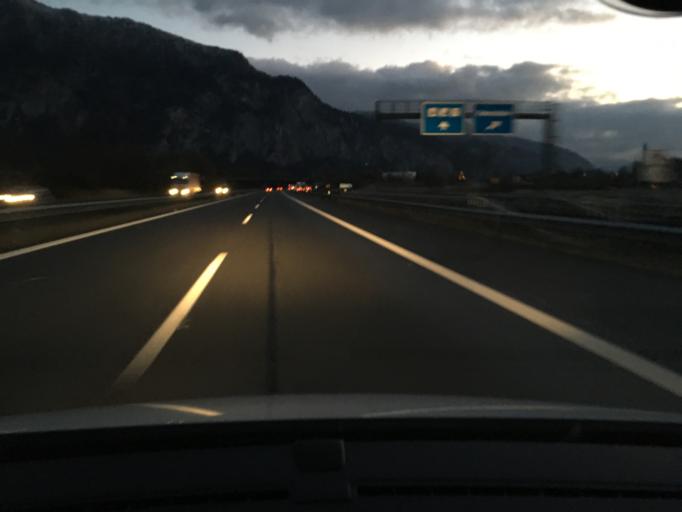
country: DE
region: Bavaria
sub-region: Upper Bavaria
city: Kiefersfelden
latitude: 47.6218
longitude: 12.2020
